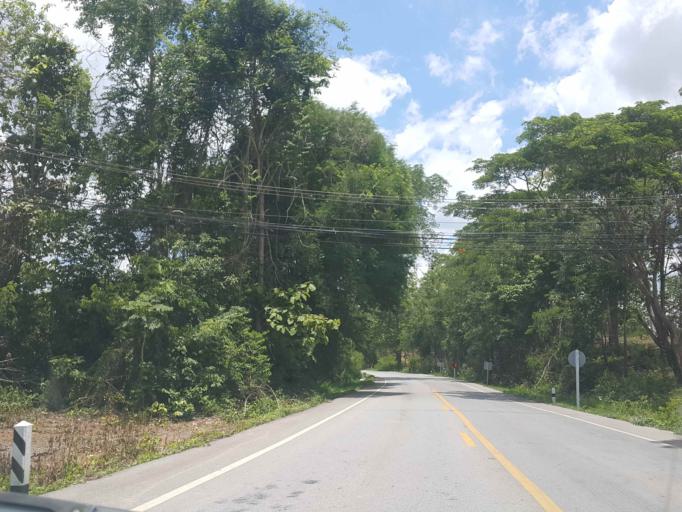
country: TH
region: Nan
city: Wiang Sa
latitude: 18.5240
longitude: 100.6125
